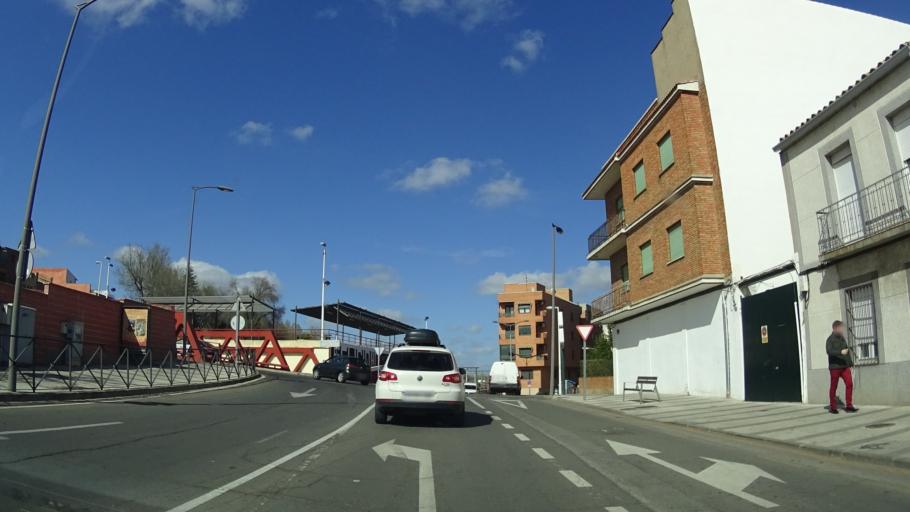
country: ES
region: Castille-La Mancha
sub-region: Provincia de Ciudad Real
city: Puertollano
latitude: 38.6870
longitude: -4.1131
